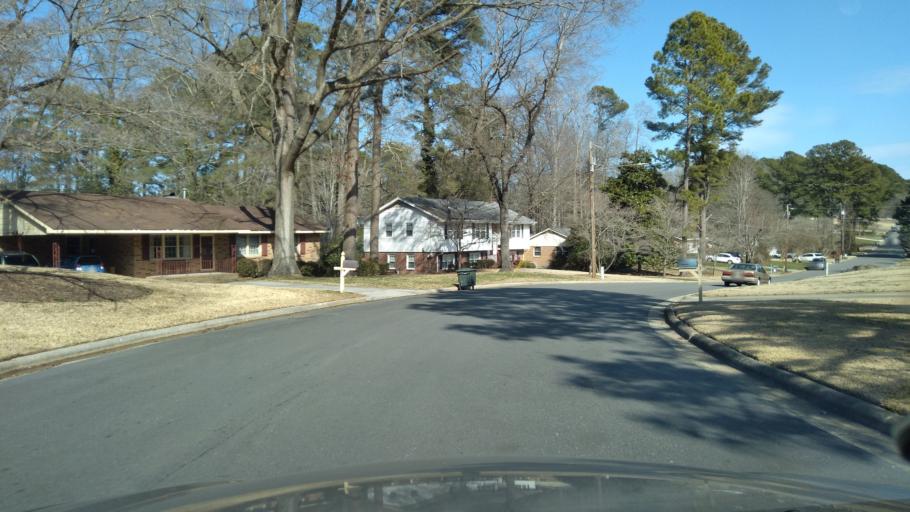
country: US
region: North Carolina
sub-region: Wake County
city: Garner
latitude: 35.6961
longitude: -78.6300
